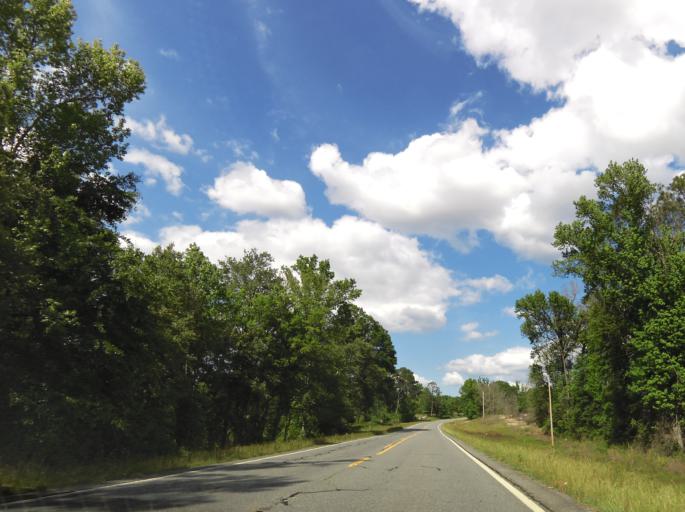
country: US
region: Georgia
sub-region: Treutlen County
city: Soperton
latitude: 32.3510
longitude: -82.6382
